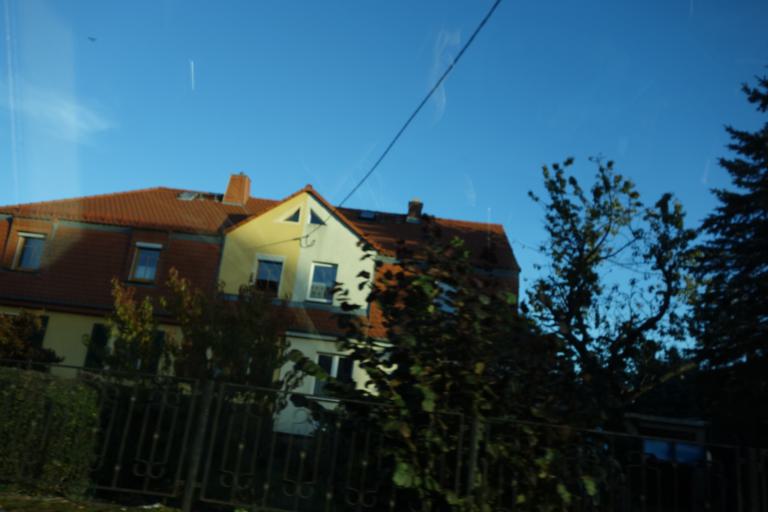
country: DE
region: Saxony
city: Freiberg
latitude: 50.8903
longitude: 13.3440
